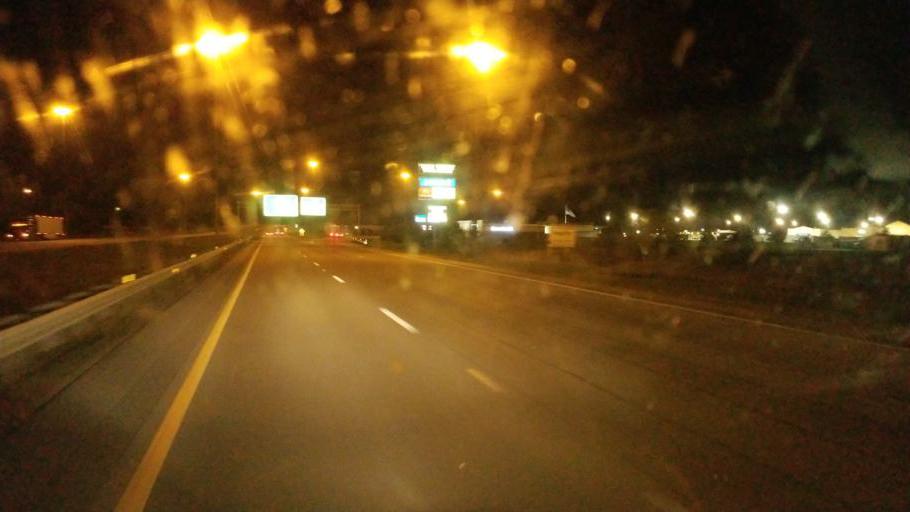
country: US
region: Ohio
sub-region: Van Wert County
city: Van Wert
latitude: 40.8857
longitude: -84.5756
